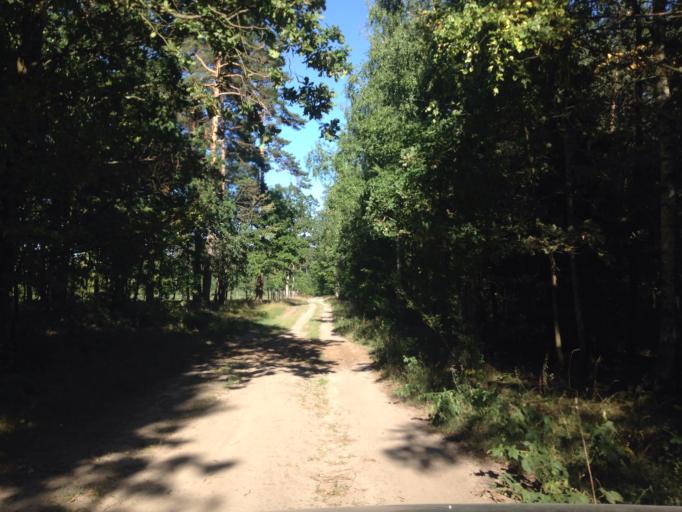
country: PL
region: Kujawsko-Pomorskie
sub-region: Powiat brodnicki
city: Gorzno
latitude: 53.1538
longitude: 19.6658
